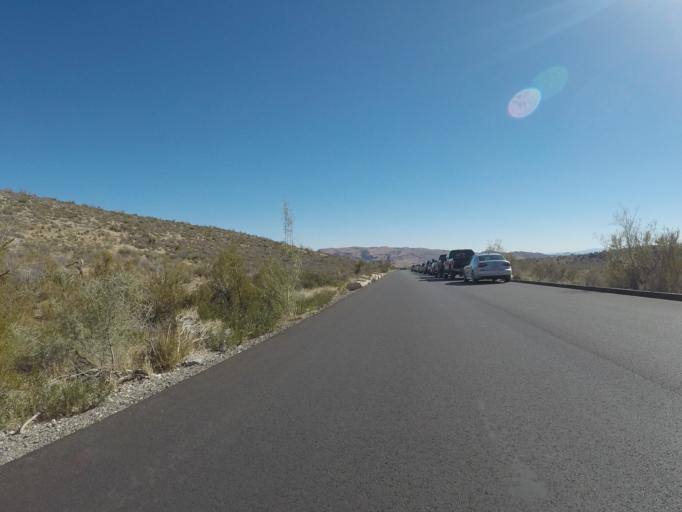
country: US
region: Nevada
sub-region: Clark County
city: Summerlin South
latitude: 36.1499
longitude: -115.4836
